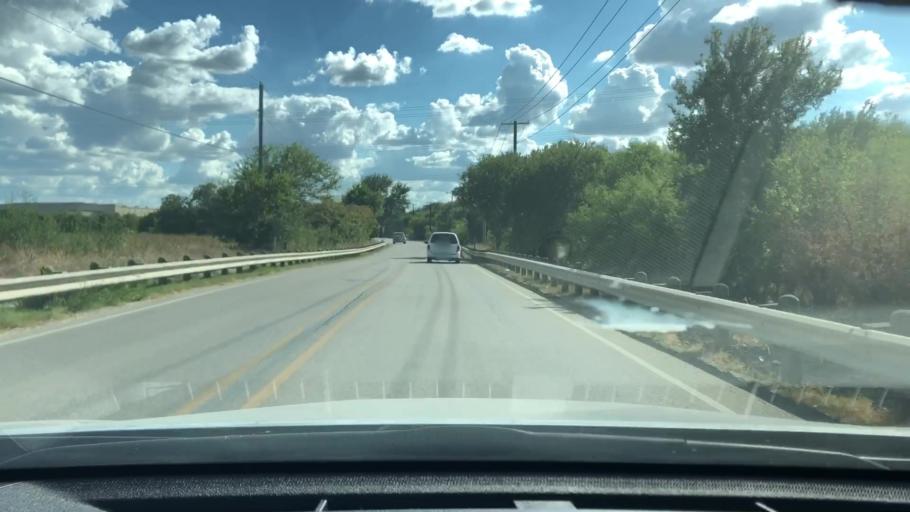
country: US
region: Texas
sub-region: Guadalupe County
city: Northcliff
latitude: 29.6514
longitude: -98.2145
